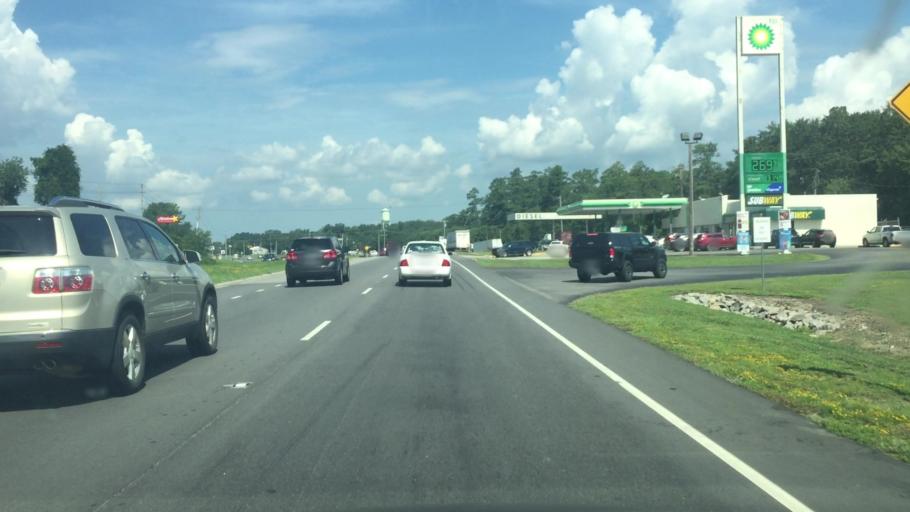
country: US
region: North Carolina
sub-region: Scotland County
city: Laurel Hill
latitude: 34.8058
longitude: -79.5422
